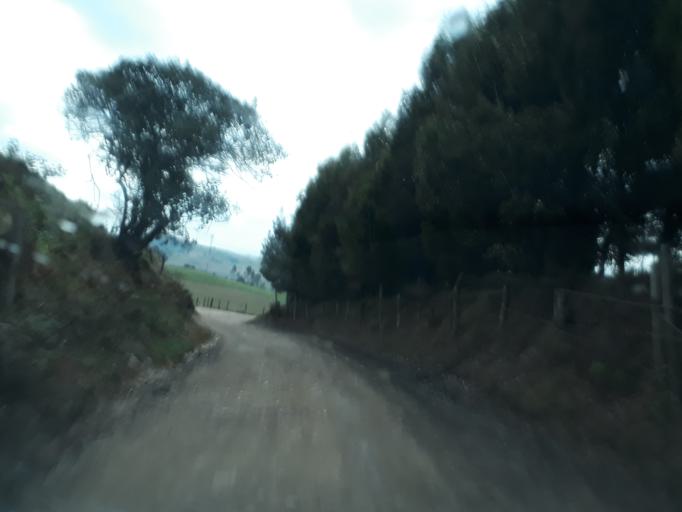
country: CO
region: Boyaca
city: Ventaquemada
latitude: 5.3076
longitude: -73.5824
